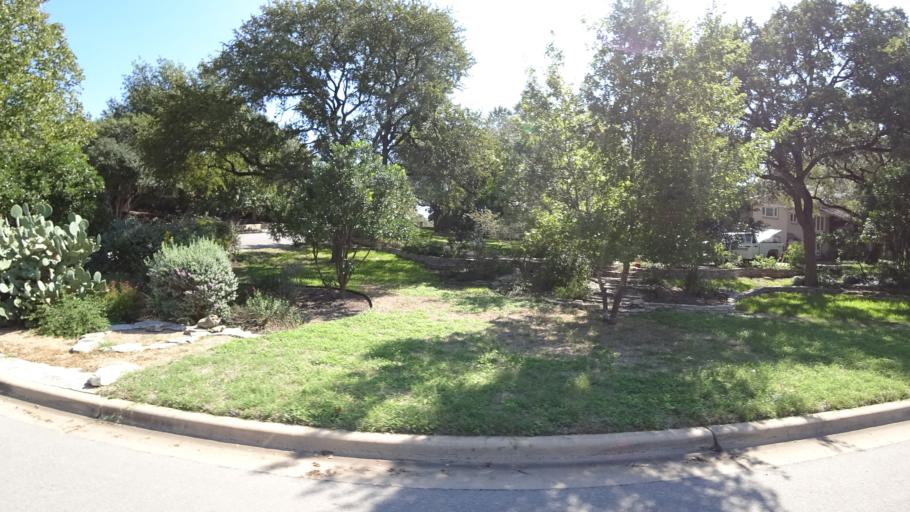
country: US
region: Texas
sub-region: Travis County
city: Rollingwood
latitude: 30.2739
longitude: -97.7802
